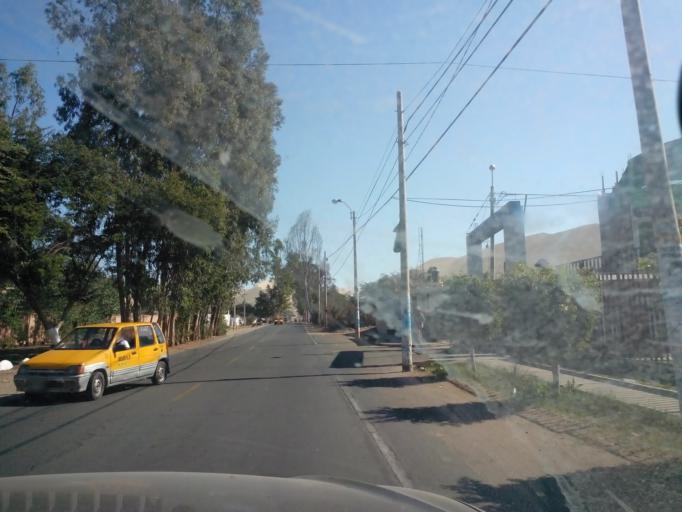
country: PE
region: Ica
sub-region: Provincia de Ica
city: Ica
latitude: -14.0823
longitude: -75.7511
